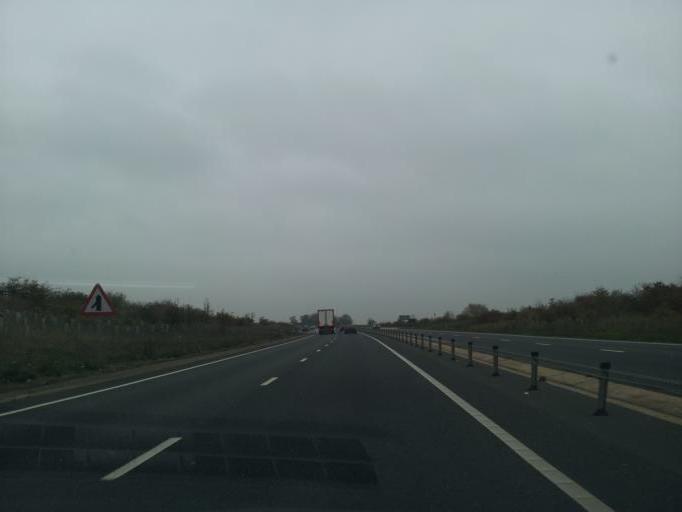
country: GB
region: England
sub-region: Bedford
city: Willington
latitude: 52.1524
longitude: -0.3840
